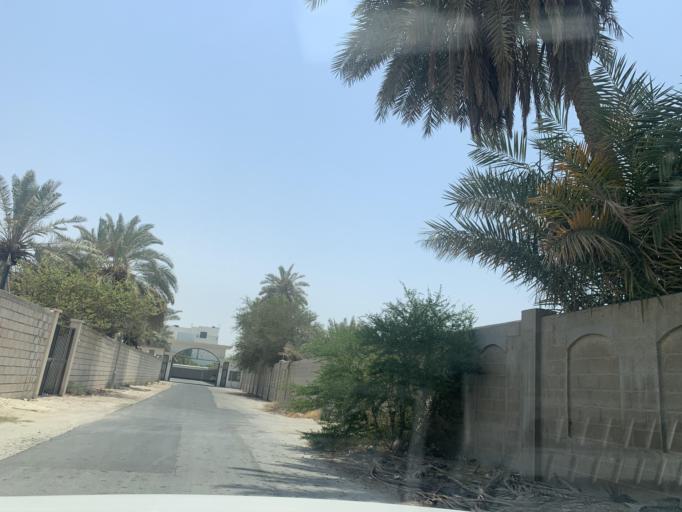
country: BH
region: Manama
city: Jidd Hafs
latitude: 26.2051
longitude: 50.4754
